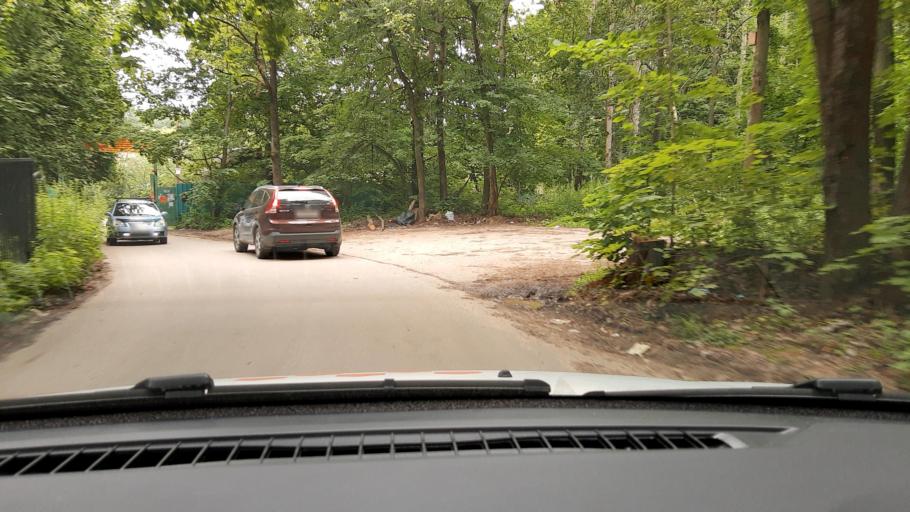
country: RU
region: Nizjnij Novgorod
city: Nizhniy Novgorod
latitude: 56.2806
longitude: 44.0063
